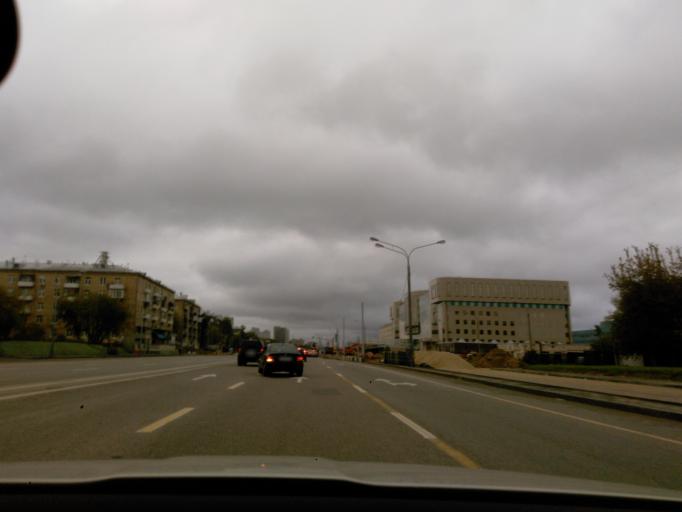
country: RU
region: Moscow
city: Strogino
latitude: 55.8269
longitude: 37.4233
